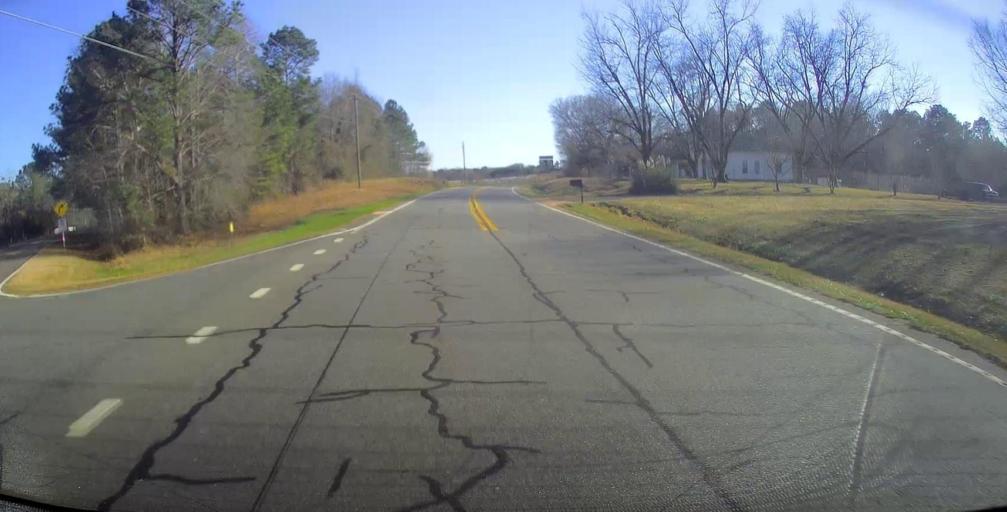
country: US
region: Georgia
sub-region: Talbot County
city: Sardis
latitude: 32.7783
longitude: -84.5580
